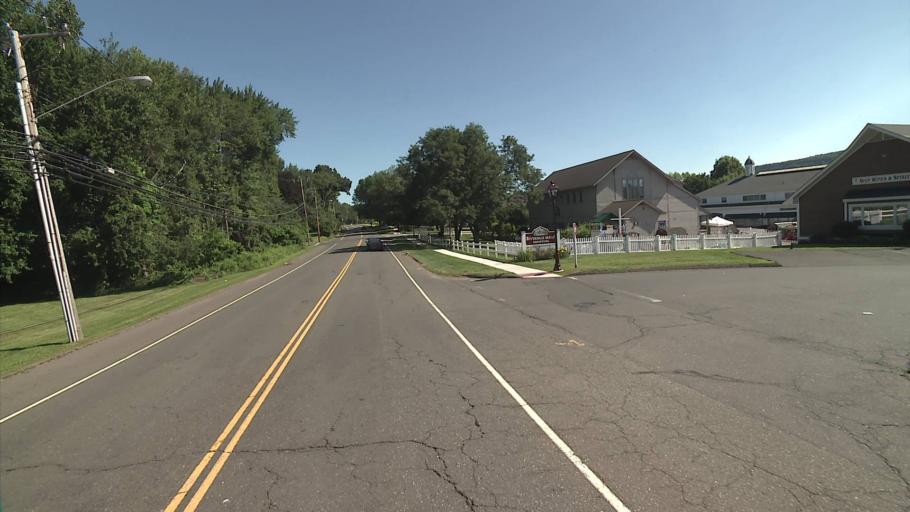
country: US
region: Connecticut
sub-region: Hartford County
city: Weatogue
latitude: 41.8195
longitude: -72.8295
